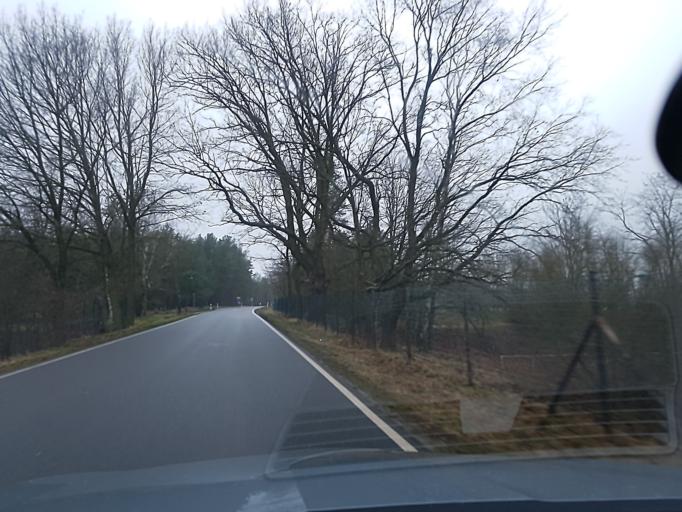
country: DE
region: Brandenburg
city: Doberlug-Kirchhain
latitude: 51.6548
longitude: 13.5178
